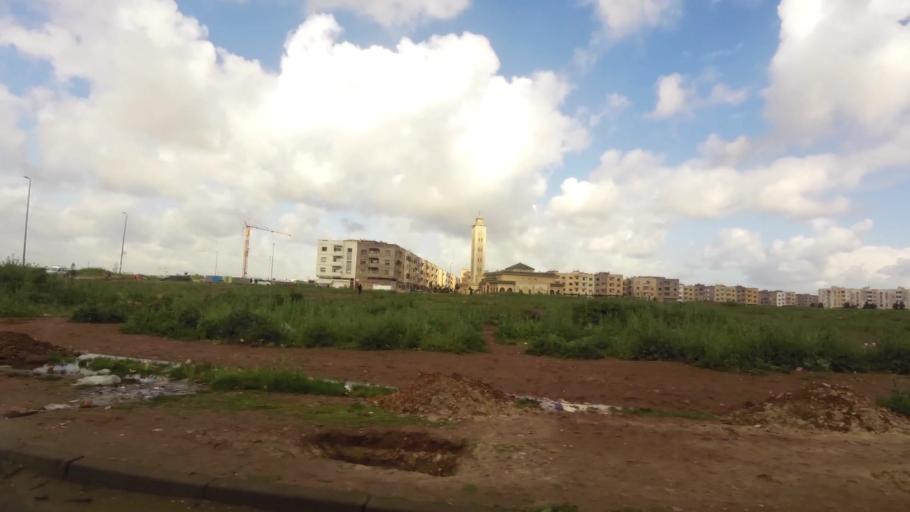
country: MA
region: Grand Casablanca
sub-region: Nouaceur
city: Bouskoura
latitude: 33.5326
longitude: -7.6999
